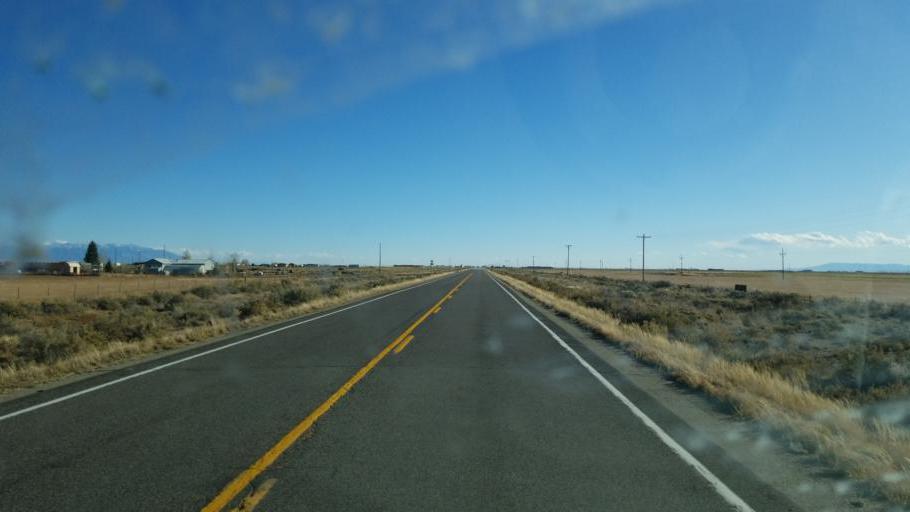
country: US
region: Colorado
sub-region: Saguache County
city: Saguache
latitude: 38.1296
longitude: -105.9230
